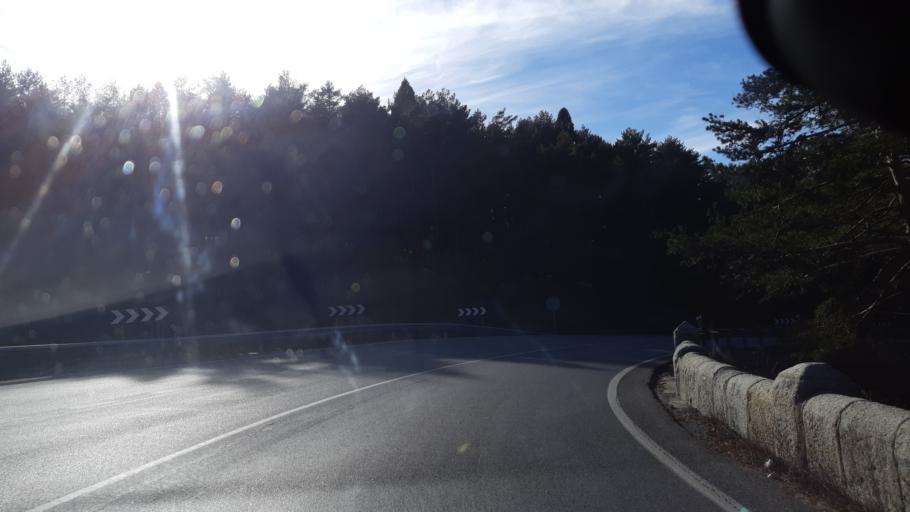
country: ES
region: Madrid
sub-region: Provincia de Madrid
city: Guadarrama
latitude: 40.7044
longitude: -4.1465
